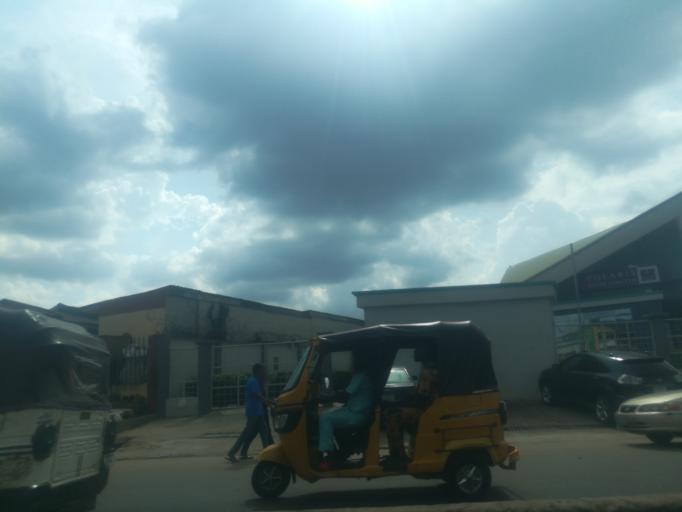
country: NG
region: Oyo
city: Ibadan
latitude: 7.4342
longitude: 3.9115
